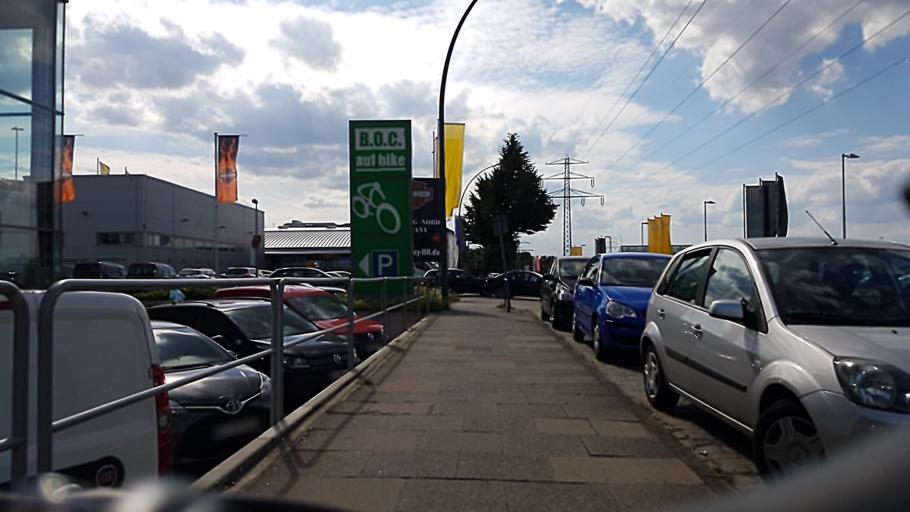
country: DE
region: Hamburg
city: Hamburg-Nord
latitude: 53.6012
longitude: 9.9773
